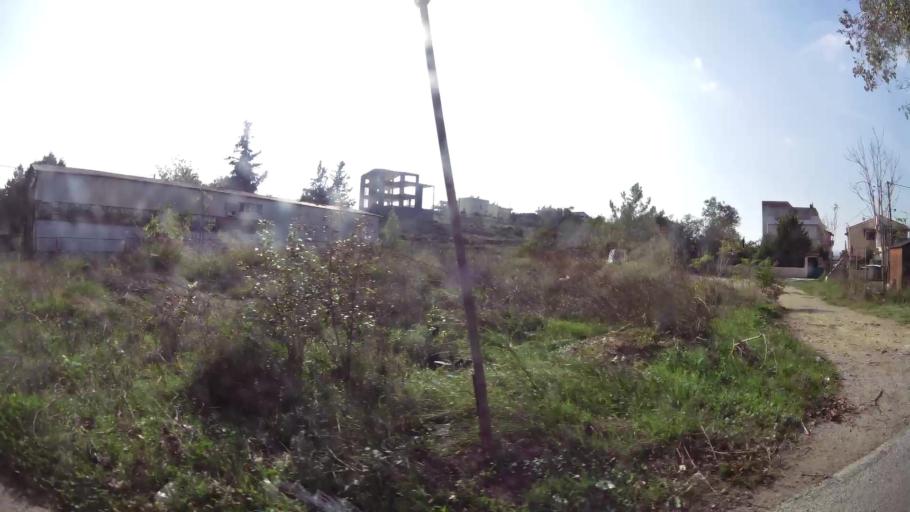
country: GR
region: Attica
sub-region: Nomarchia Anatolikis Attikis
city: Acharnes
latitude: 38.0710
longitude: 23.7318
